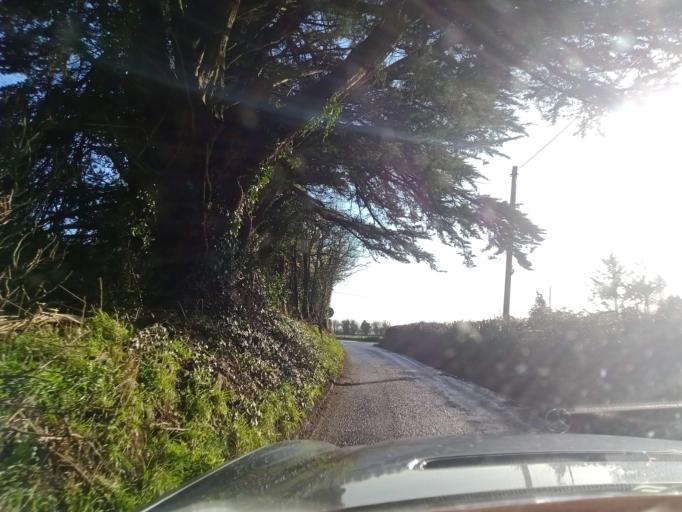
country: IE
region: Leinster
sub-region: Kilkenny
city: Mooncoin
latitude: 52.2846
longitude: -7.1893
